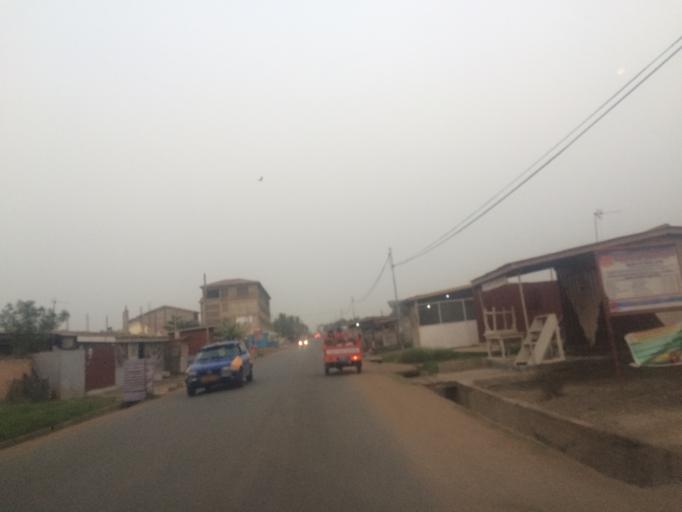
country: GH
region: Greater Accra
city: Teshi Old Town
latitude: 5.5991
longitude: -0.0981
